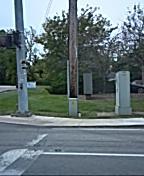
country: US
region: Kentucky
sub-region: Jefferson County
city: Douglass Hills
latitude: 38.2455
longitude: -85.5649
